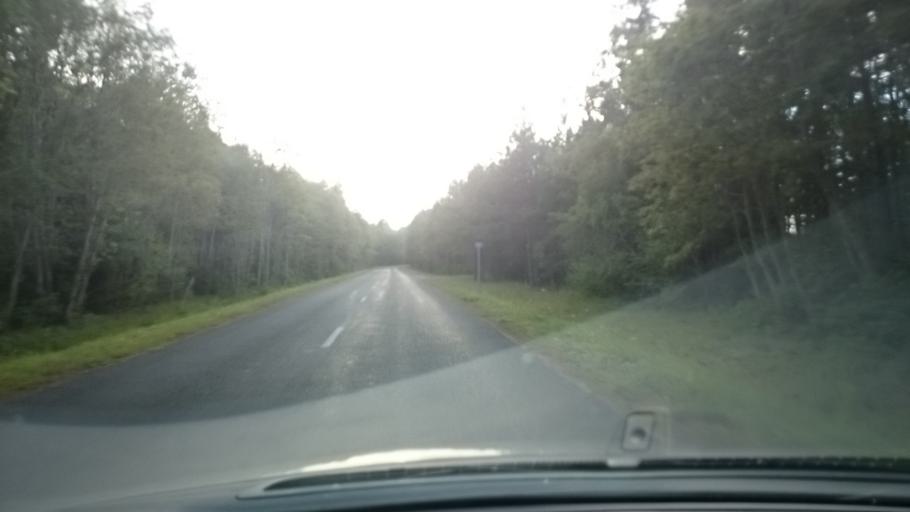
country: EE
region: Saare
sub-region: Kuressaare linn
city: Kuressaare
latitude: 58.4157
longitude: 22.0846
